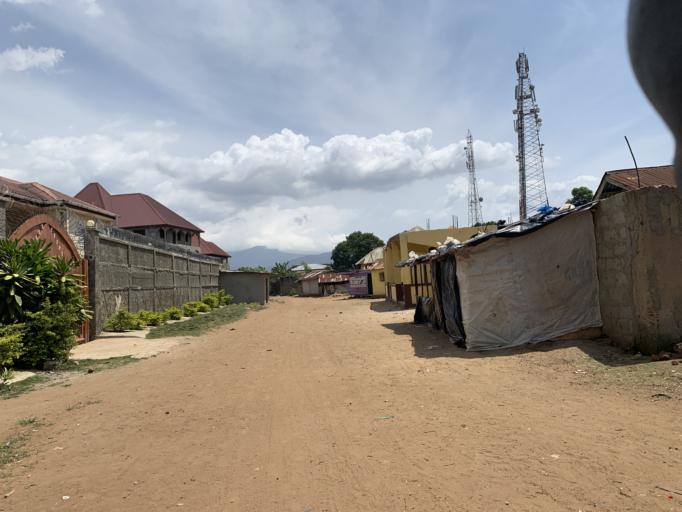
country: SL
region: Western Area
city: Waterloo
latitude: 8.3360
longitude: -13.0385
